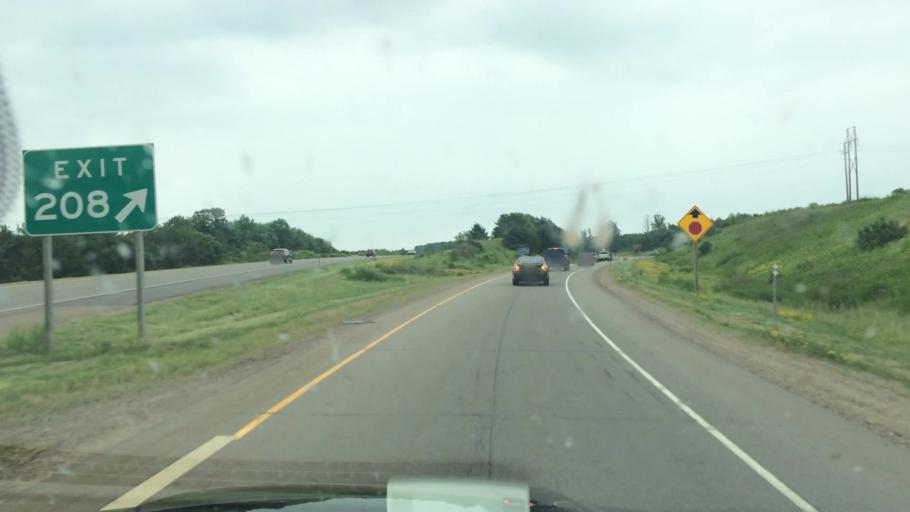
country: US
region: Wisconsin
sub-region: Lincoln County
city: Merrill
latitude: 45.1737
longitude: -89.6460
